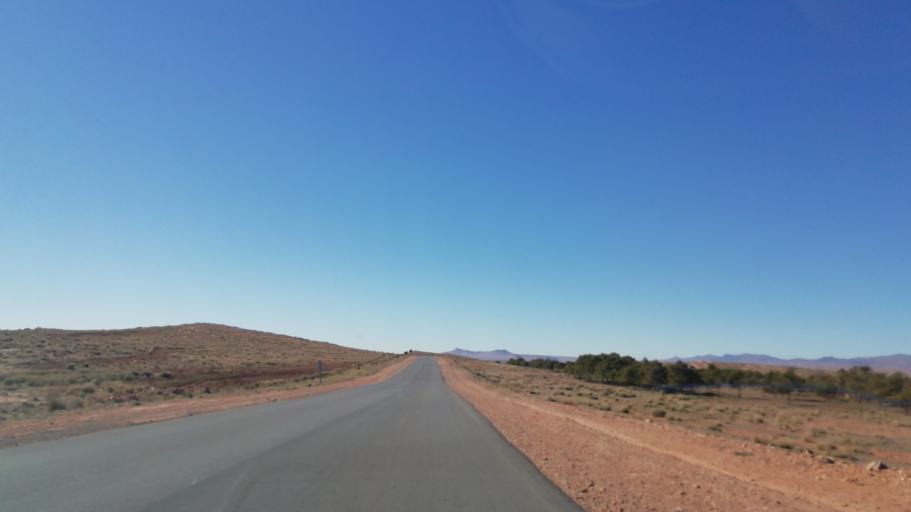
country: DZ
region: El Bayadh
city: El Bayadh
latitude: 33.6410
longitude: 1.3876
